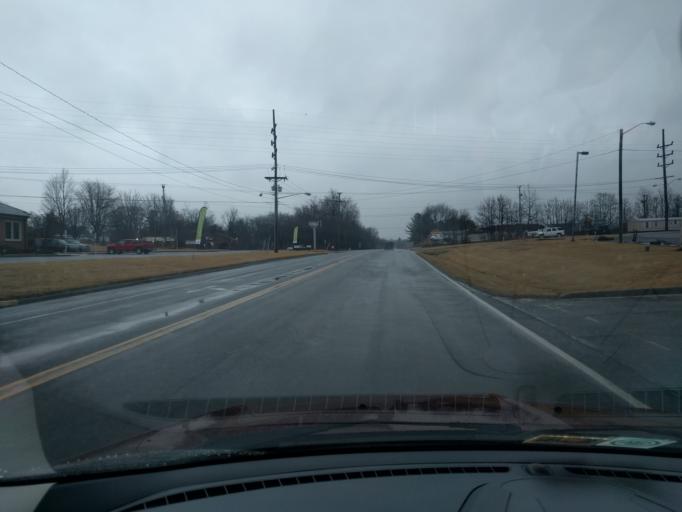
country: US
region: Virginia
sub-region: Pulaski County
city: Pulaski
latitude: 37.0478
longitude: -80.7543
